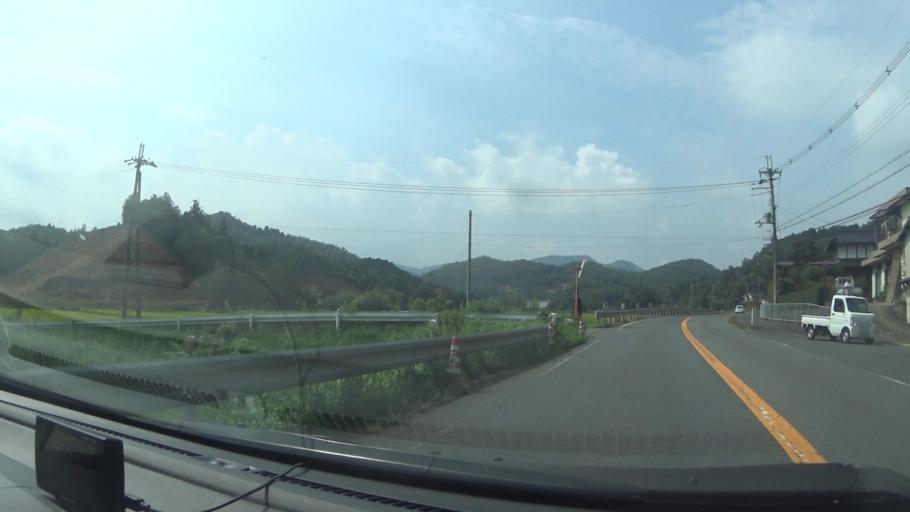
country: JP
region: Kyoto
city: Ayabe
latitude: 35.1756
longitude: 135.3634
